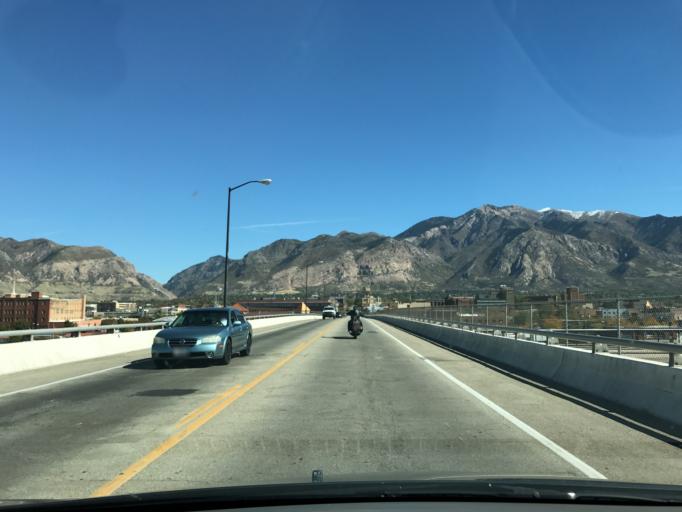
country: US
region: Utah
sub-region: Weber County
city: Ogden
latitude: 41.2229
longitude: -111.9819
